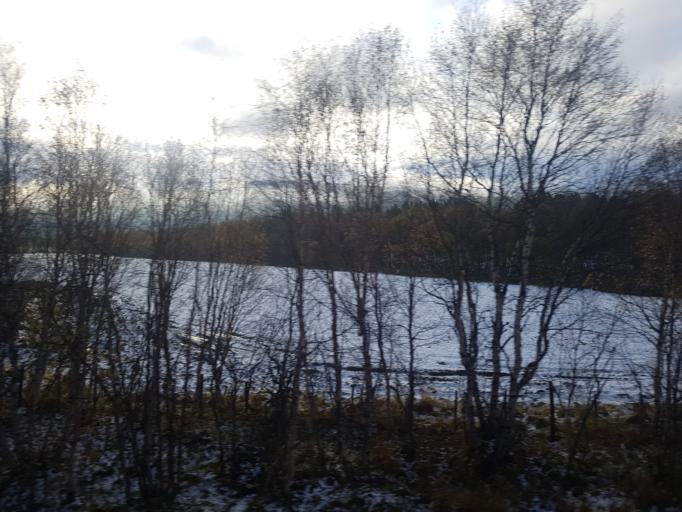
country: NO
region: Sor-Trondelag
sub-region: Oppdal
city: Oppdal
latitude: 62.6380
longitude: 9.8055
